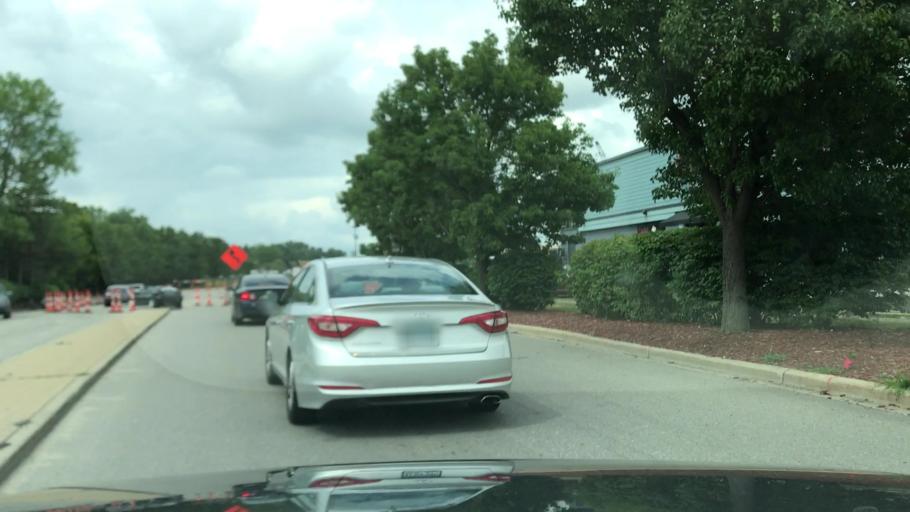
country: US
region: Michigan
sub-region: Kent County
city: East Grand Rapids
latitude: 42.9127
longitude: -85.5918
